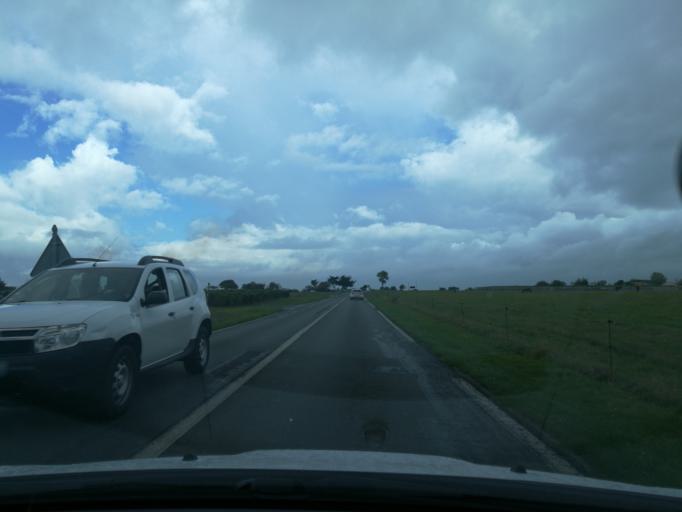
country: FR
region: Poitou-Charentes
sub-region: Departement de la Charente-Maritime
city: Saint-Martin-de-Re
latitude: 46.1989
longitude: -1.3722
